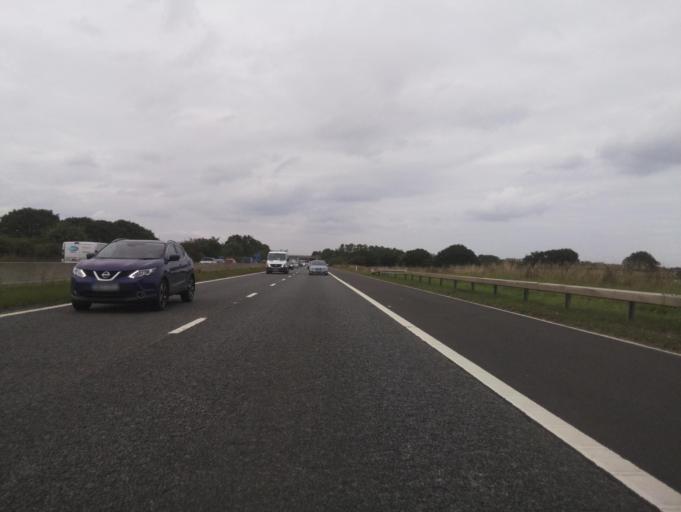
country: GB
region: England
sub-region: County Durham
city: West Rainton
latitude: 54.8127
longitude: -1.5223
